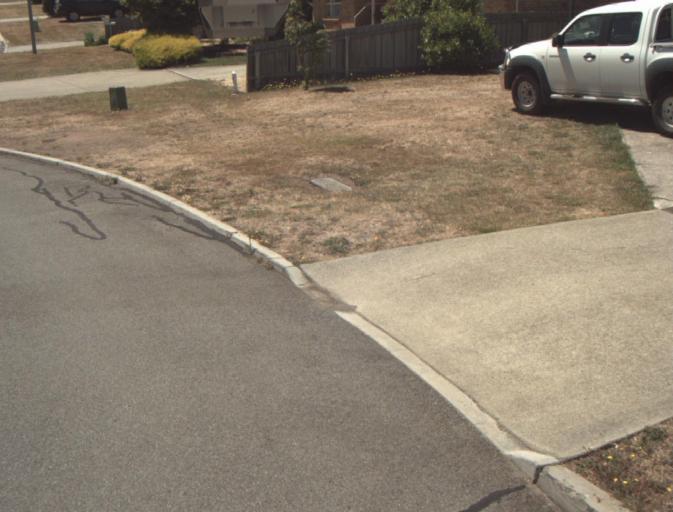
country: AU
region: Tasmania
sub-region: Launceston
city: Mayfield
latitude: -41.3859
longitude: 147.1164
